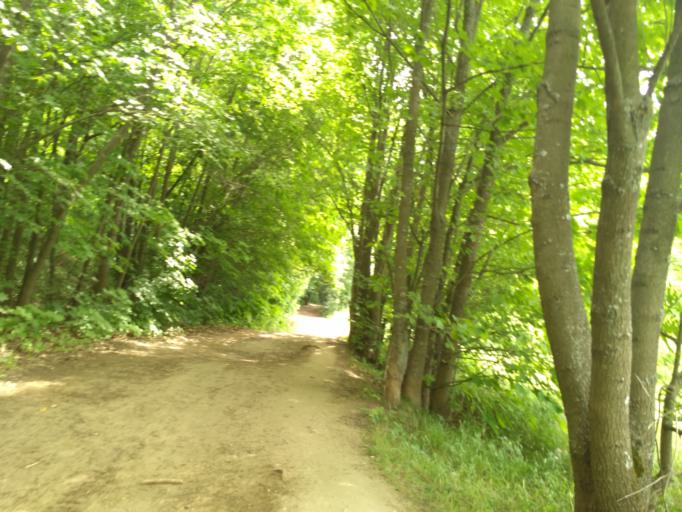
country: RU
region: Nizjnij Novgorod
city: Nizhniy Novgorod
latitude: 56.2644
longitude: 43.9720
